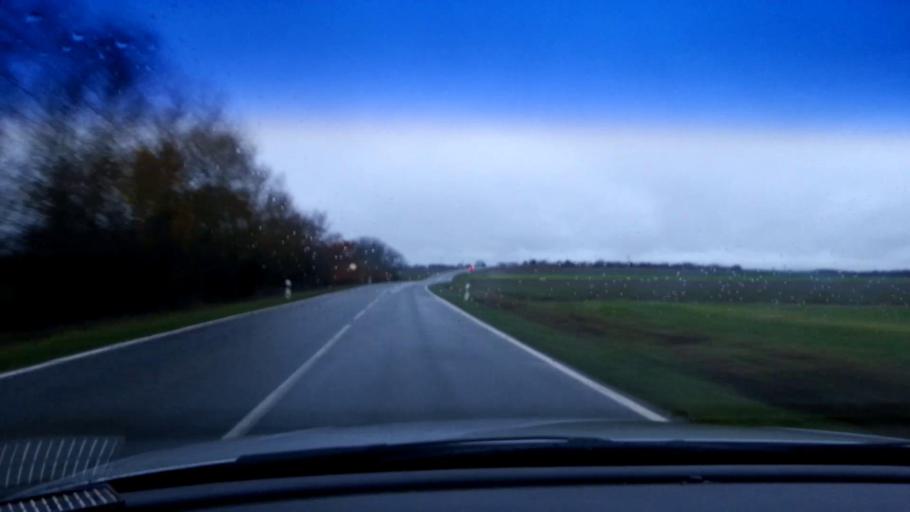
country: DE
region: Bavaria
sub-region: Upper Franconia
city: Zapfendorf
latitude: 49.9842
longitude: 10.9544
